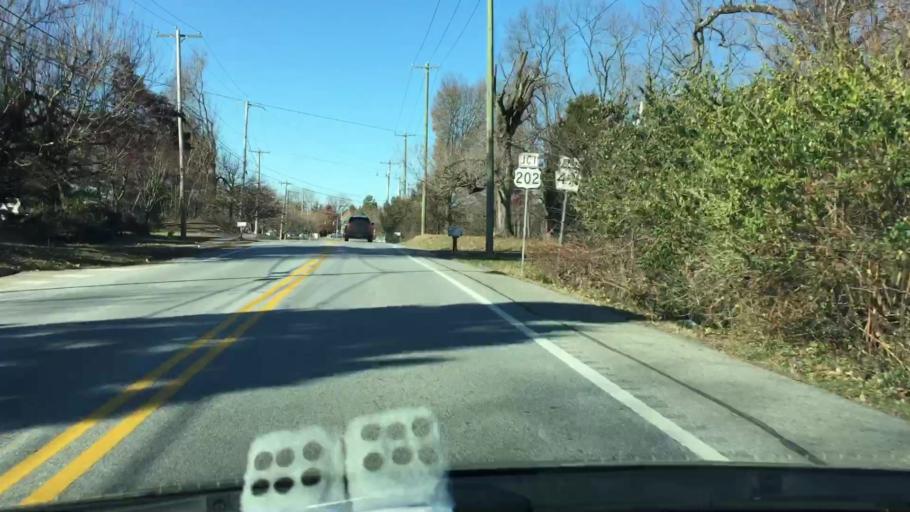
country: US
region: Pennsylvania
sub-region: Delaware County
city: Chester Heights
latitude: 39.8484
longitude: -75.5347
